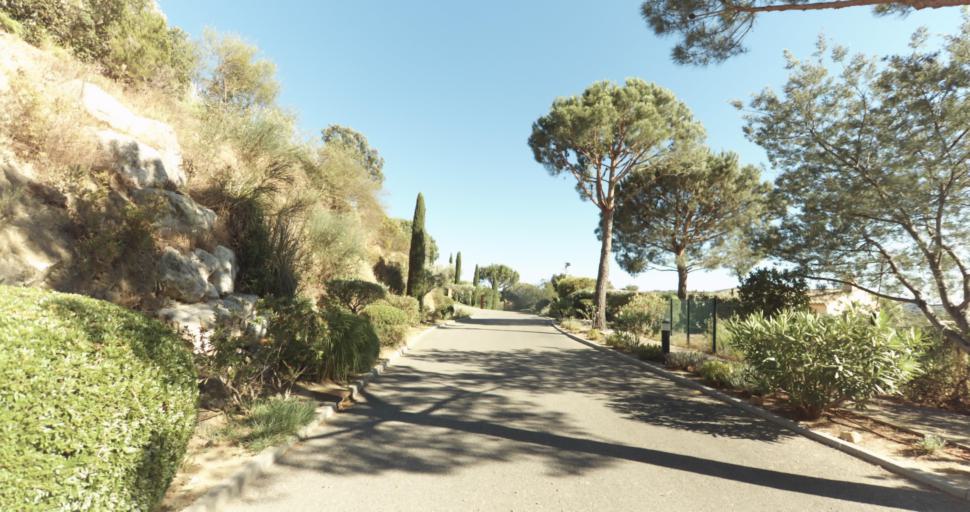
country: FR
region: Provence-Alpes-Cote d'Azur
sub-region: Departement du Var
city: Gassin
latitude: 43.2564
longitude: 6.6067
